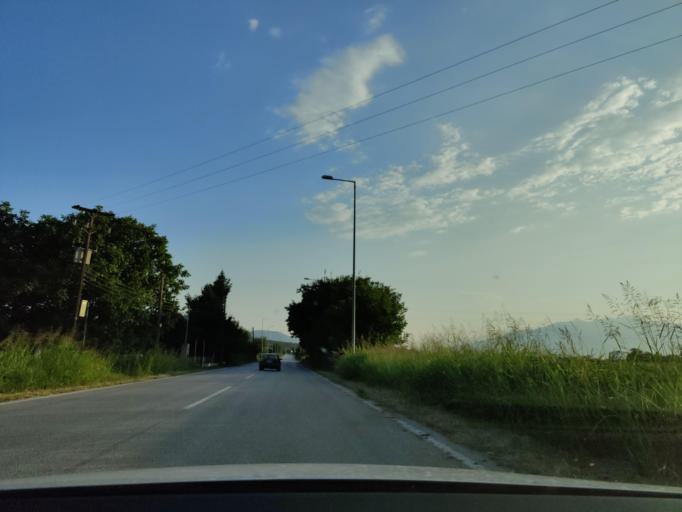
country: GR
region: East Macedonia and Thrace
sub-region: Nomos Kavalas
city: Amygdaleonas
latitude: 40.9822
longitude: 24.3688
